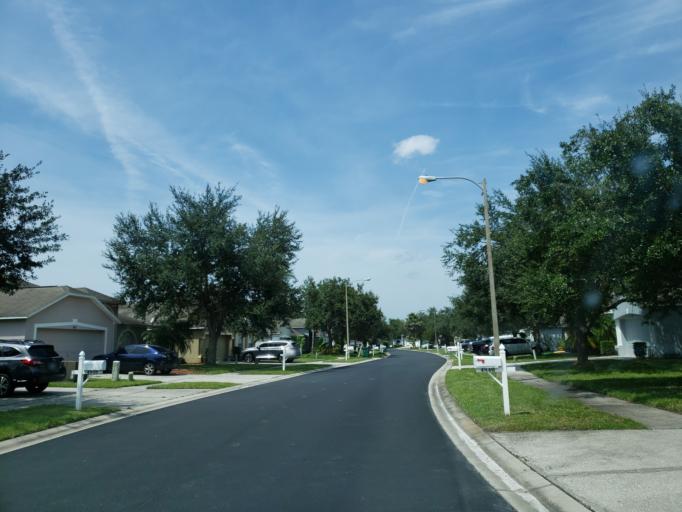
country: US
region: Florida
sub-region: Pasco County
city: Land O' Lakes
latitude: 28.2274
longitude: -82.3926
